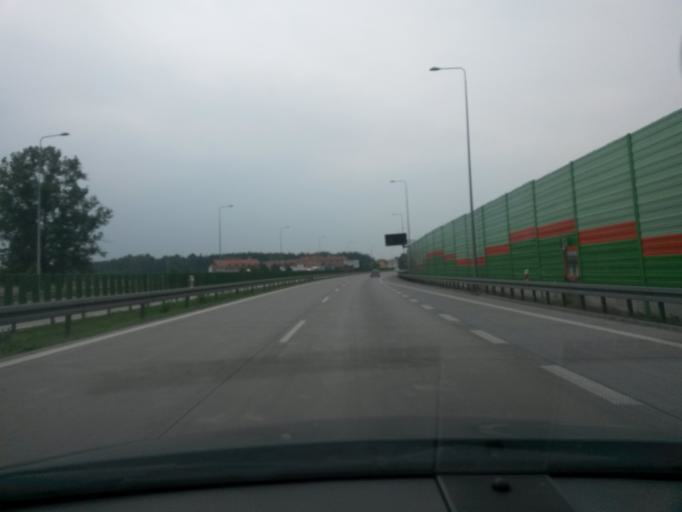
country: PL
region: Lodz Voivodeship
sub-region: Powiat piotrkowski
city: Wolborz
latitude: 51.5078
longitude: 19.8913
